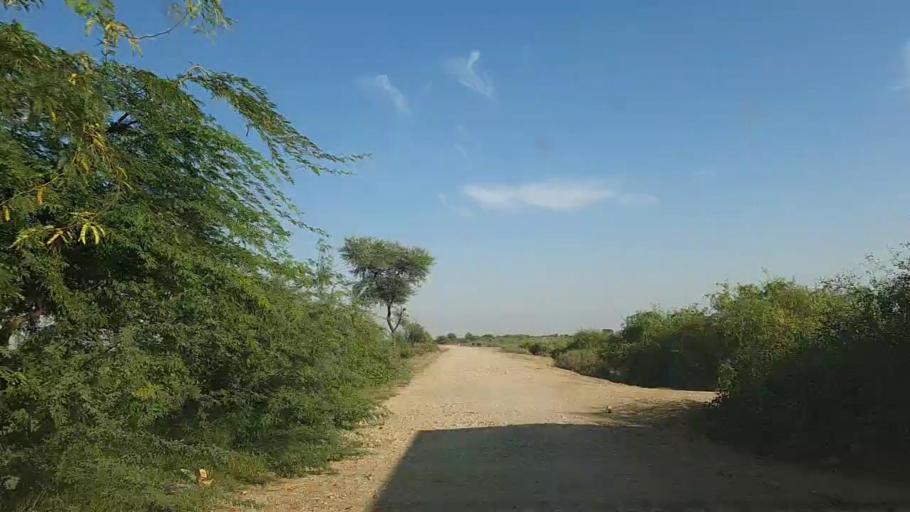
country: PK
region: Sindh
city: Mirpur Batoro
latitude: 24.7616
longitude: 68.3583
